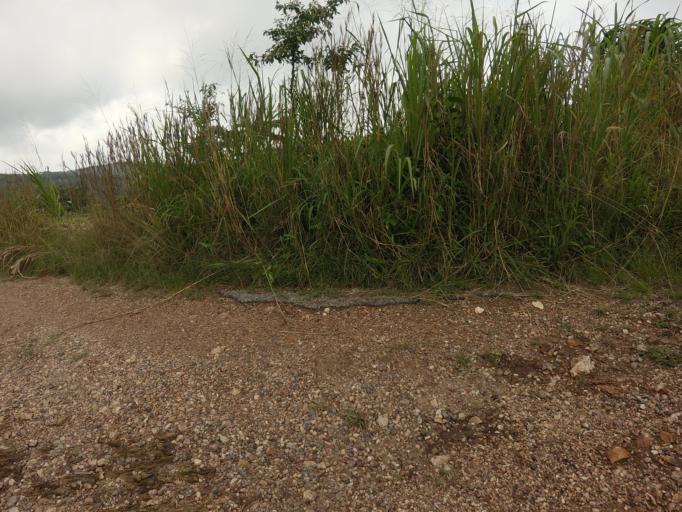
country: GH
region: Volta
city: Kpandu
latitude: 6.8402
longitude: 0.4317
